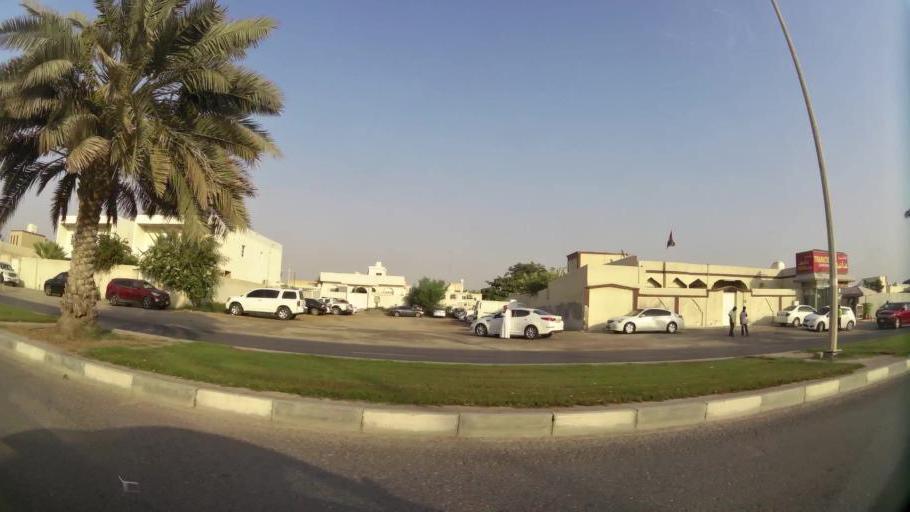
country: AE
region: Ajman
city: Ajman
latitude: 25.3767
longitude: 55.4331
